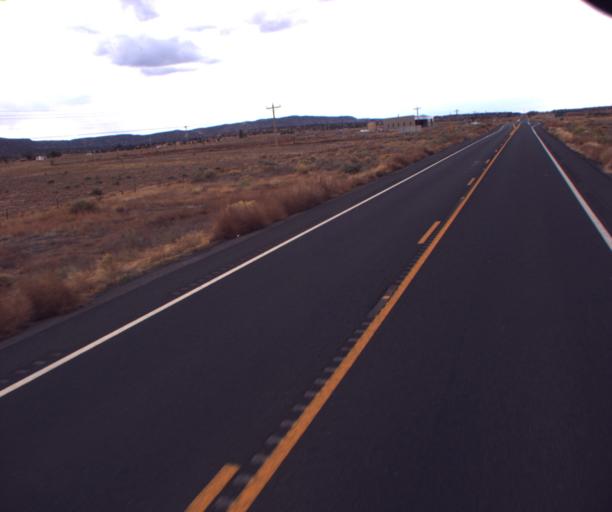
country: US
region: Arizona
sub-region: Coconino County
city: Kaibito
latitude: 36.4627
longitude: -110.6886
